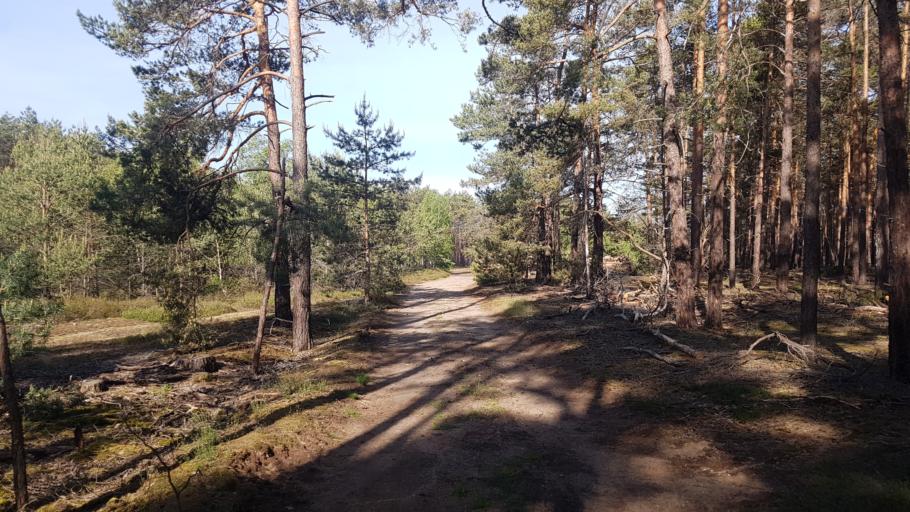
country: DE
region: Brandenburg
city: Doberlug-Kirchhain
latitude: 51.6152
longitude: 13.6248
